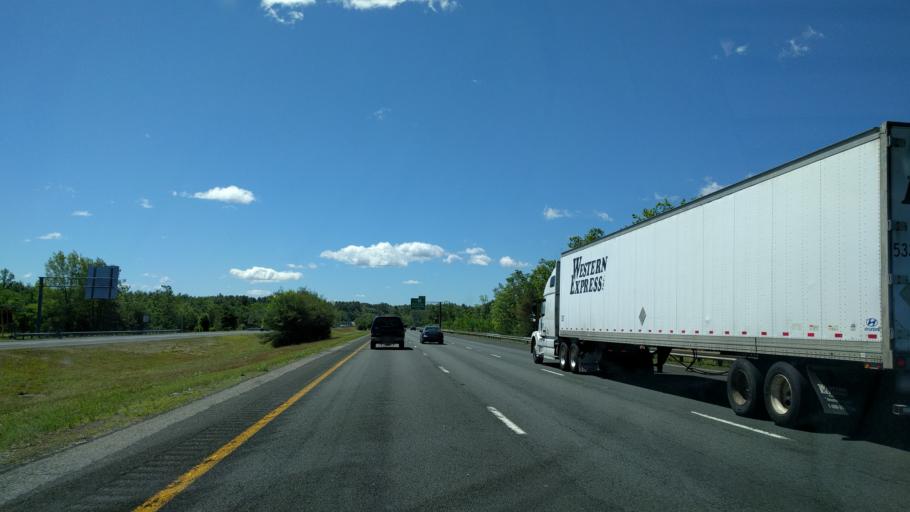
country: US
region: Massachusetts
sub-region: Worcester County
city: Sturbridge
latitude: 42.1029
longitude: -72.0850
